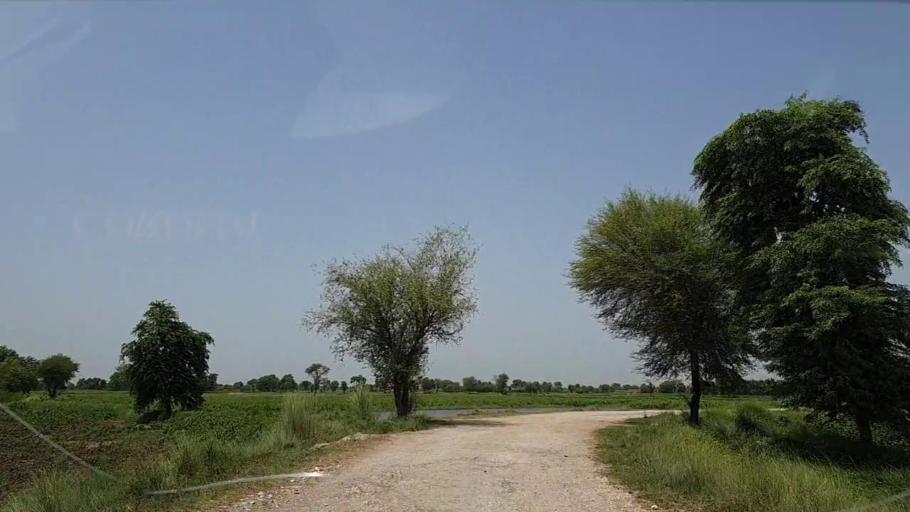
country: PK
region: Sindh
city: Tharu Shah
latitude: 26.9300
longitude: 68.0511
